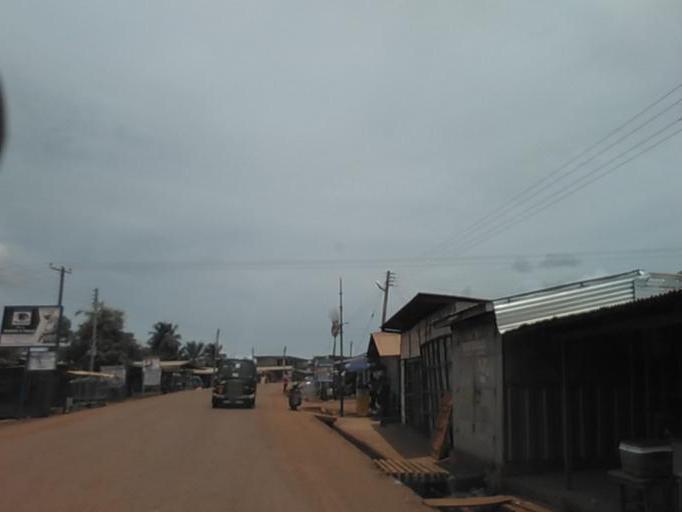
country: GH
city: Akropong
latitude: 6.1222
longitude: -0.0023
